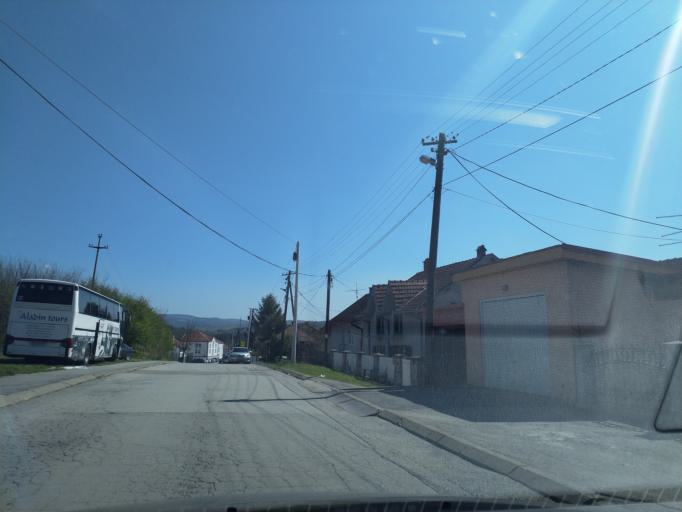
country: RS
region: Central Serbia
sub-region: Kolubarski Okrug
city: Valjevo
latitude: 44.2769
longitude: 19.8706
